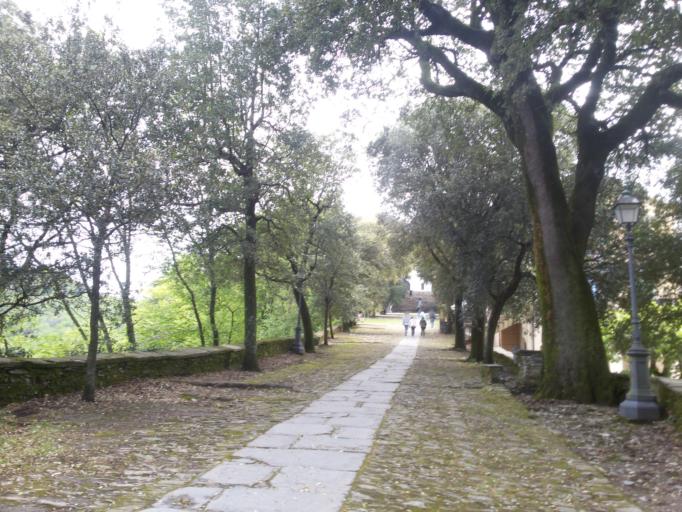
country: IT
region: Liguria
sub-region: Provincia di Genova
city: Coreglia Ligure
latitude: 44.3694
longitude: 9.2543
